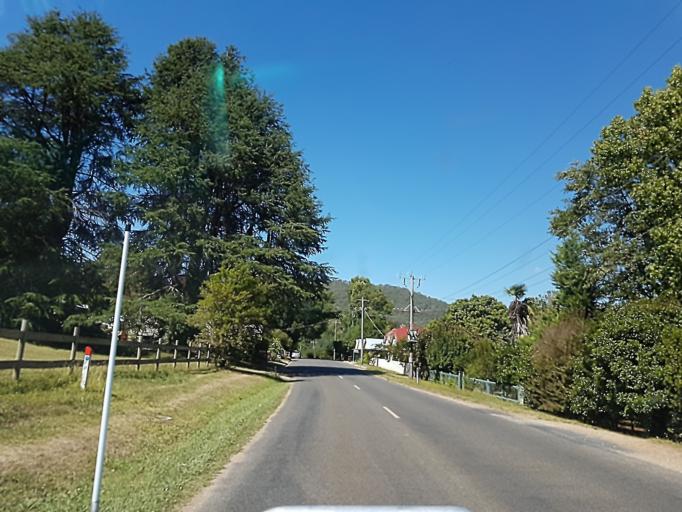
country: AU
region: Victoria
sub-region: Alpine
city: Mount Beauty
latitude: -36.7721
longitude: 146.9819
